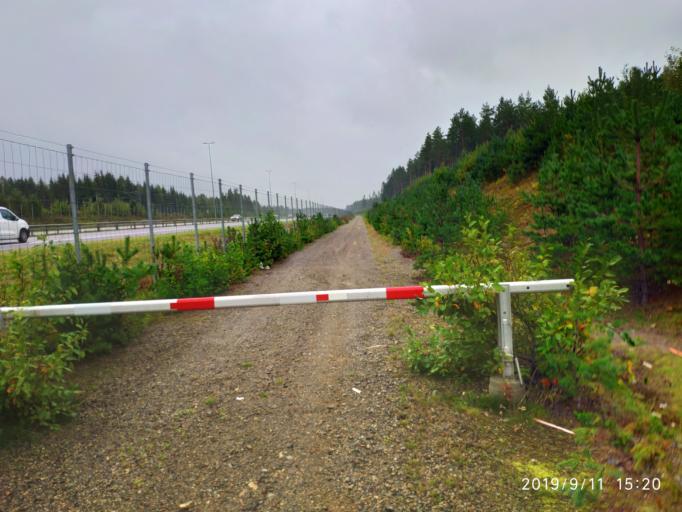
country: NO
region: Akershus
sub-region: Eidsvoll
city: Raholt
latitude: 60.2180
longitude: 11.1805
